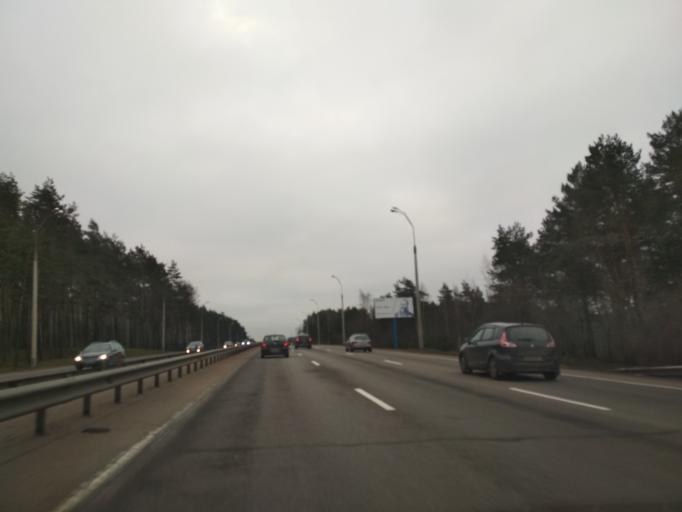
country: BY
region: Minsk
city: Vyaliki Trastsyanets
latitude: 53.8301
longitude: 27.7426
